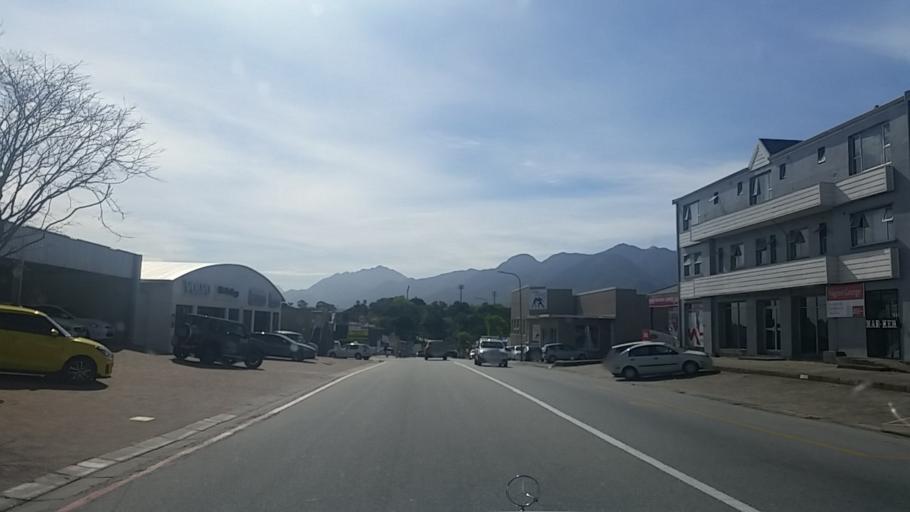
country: ZA
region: Western Cape
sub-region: Eden District Municipality
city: George
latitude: -33.9577
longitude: 22.4548
